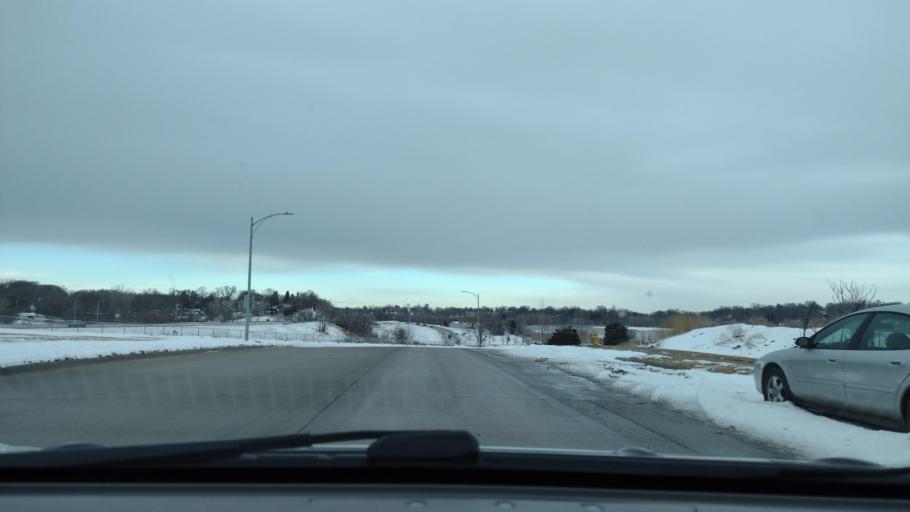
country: US
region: Nebraska
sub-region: Sarpy County
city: Offutt Air Force Base
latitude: 41.1806
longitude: -95.9373
